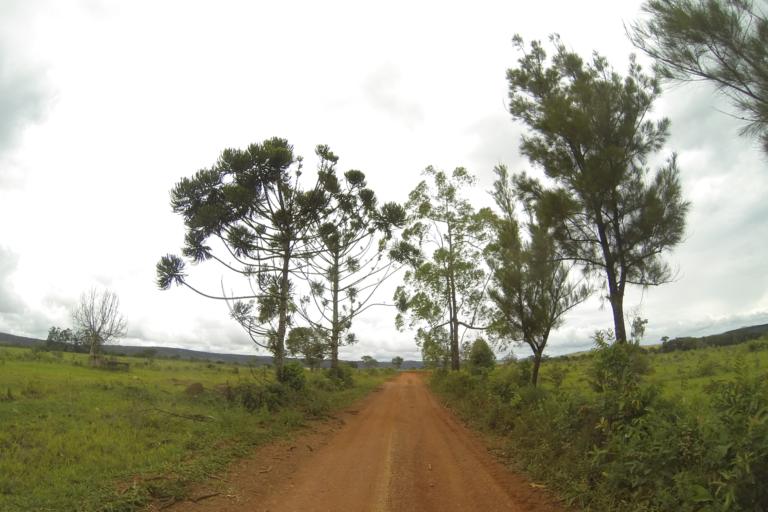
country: BR
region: Minas Gerais
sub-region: Ibia
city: Ibia
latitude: -19.7344
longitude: -46.6079
